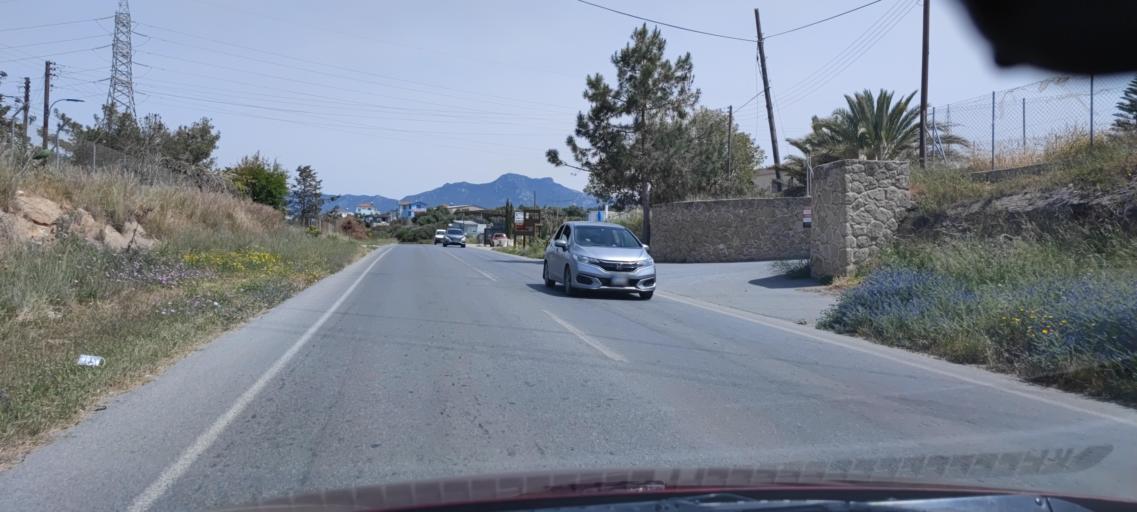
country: CY
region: Keryneia
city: Kyrenia
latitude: 35.3308
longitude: 33.4587
